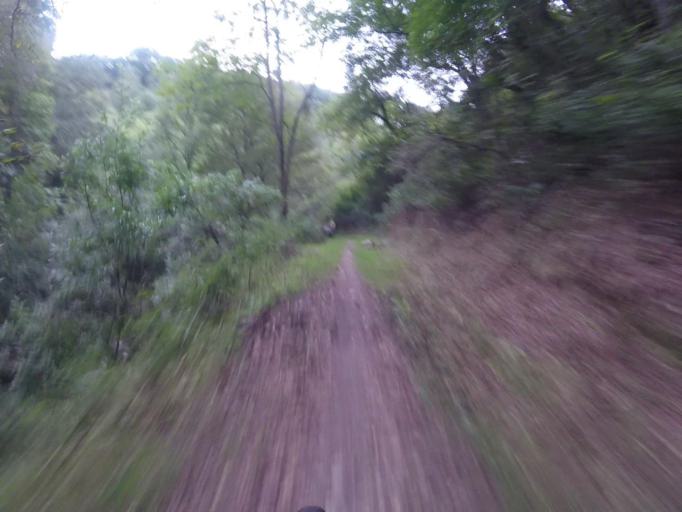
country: ES
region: Basque Country
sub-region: Provincia de Guipuzcoa
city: Errenteria
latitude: 43.2760
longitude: -1.8434
